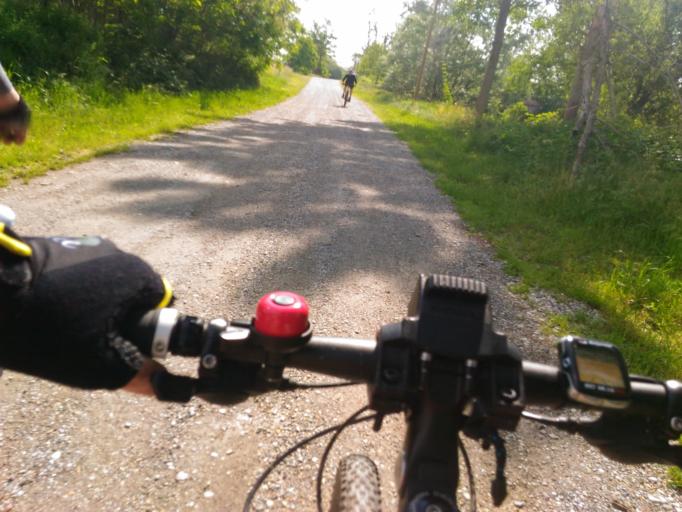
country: IT
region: Lombardy
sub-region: Provincia di Lodi
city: San Martino in Strada
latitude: 45.2641
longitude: 9.5360
